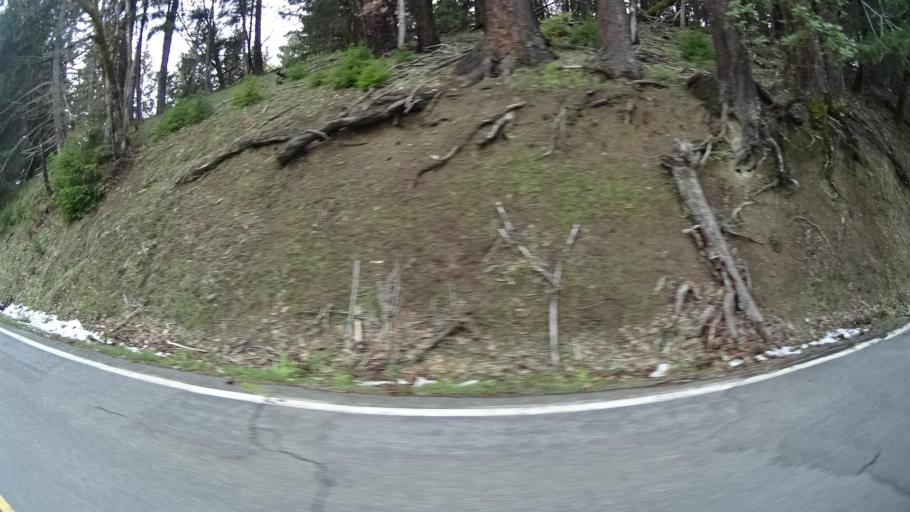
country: US
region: California
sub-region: Humboldt County
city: Willow Creek
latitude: 40.8839
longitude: -123.7713
